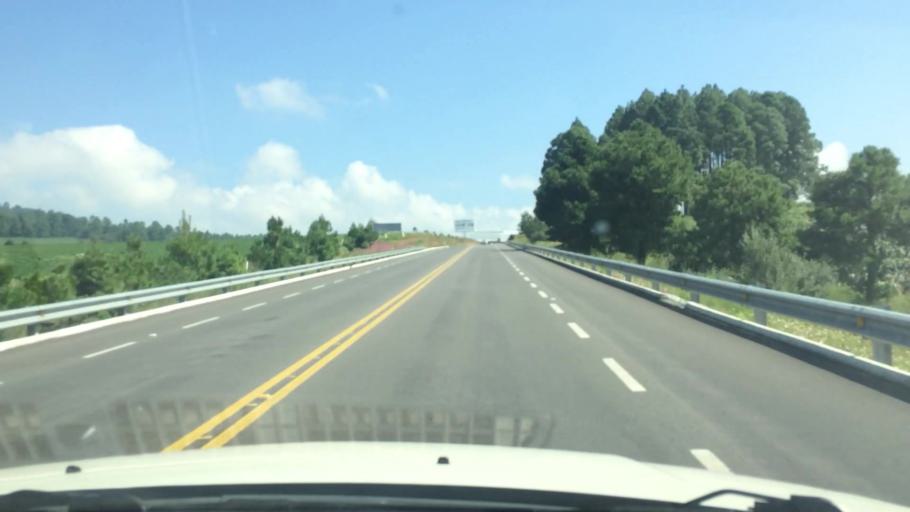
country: MX
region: Mexico
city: Amanalco de Becerra
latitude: 19.3010
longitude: -100.0111
